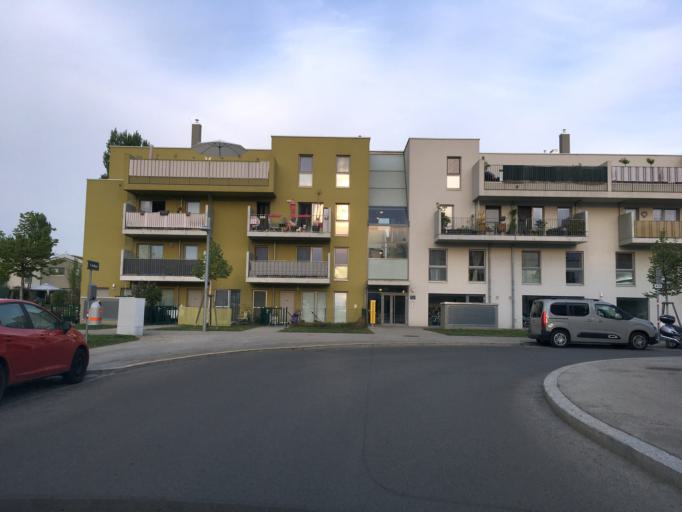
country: AT
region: Lower Austria
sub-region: Politischer Bezirk Wien-Umgebung
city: Gerasdorf bei Wien
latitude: 48.2878
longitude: 16.4347
